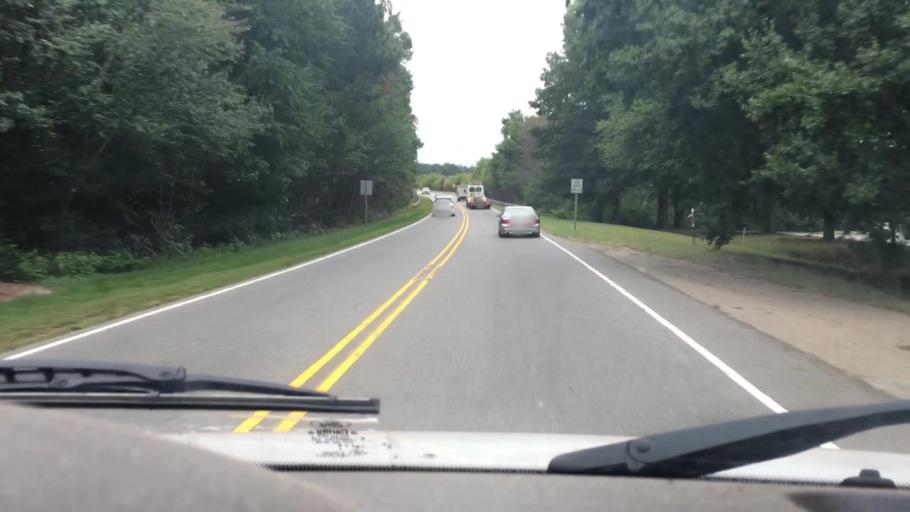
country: US
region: North Carolina
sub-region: Catawba County
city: Lake Norman of Catawba
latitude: 35.6061
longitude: -80.9368
